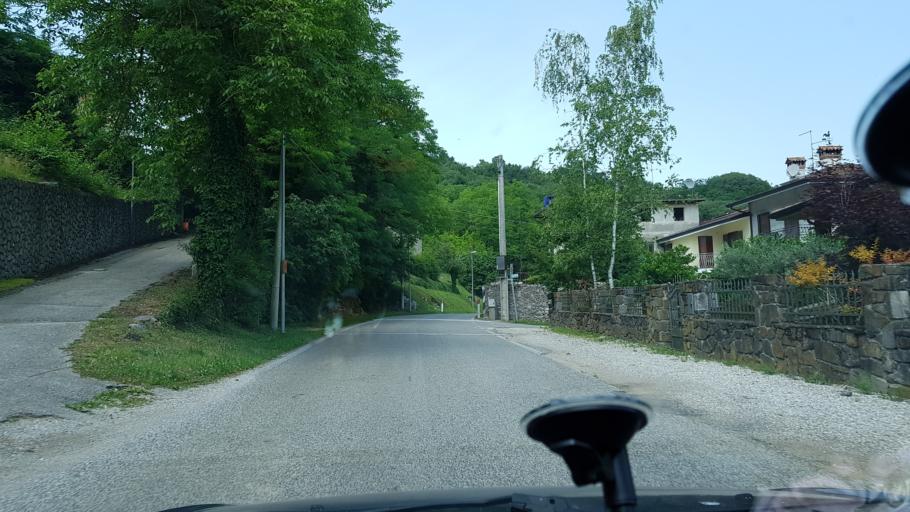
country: IT
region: Friuli Venezia Giulia
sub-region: Provincia di Gorizia
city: Savogna d'Isonzo
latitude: 45.8921
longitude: 13.5742
